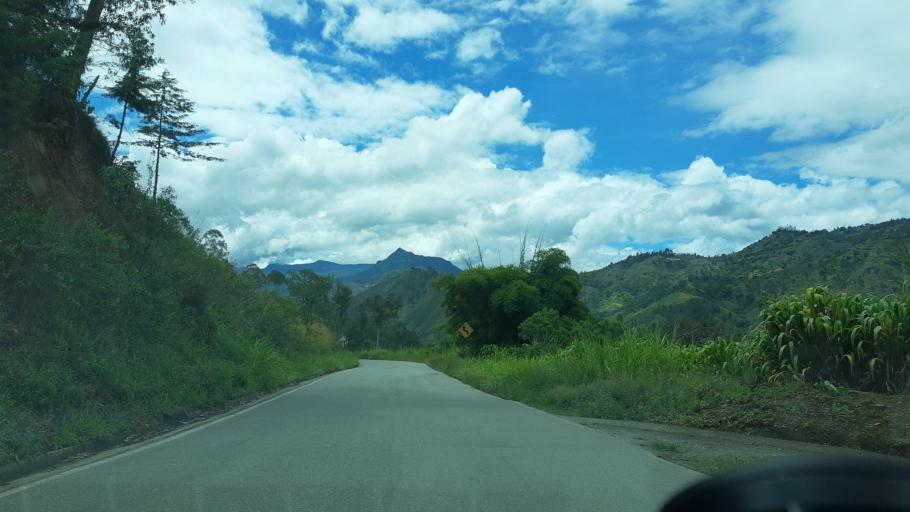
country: CO
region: Boyaca
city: Garagoa
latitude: 5.0520
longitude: -73.3869
